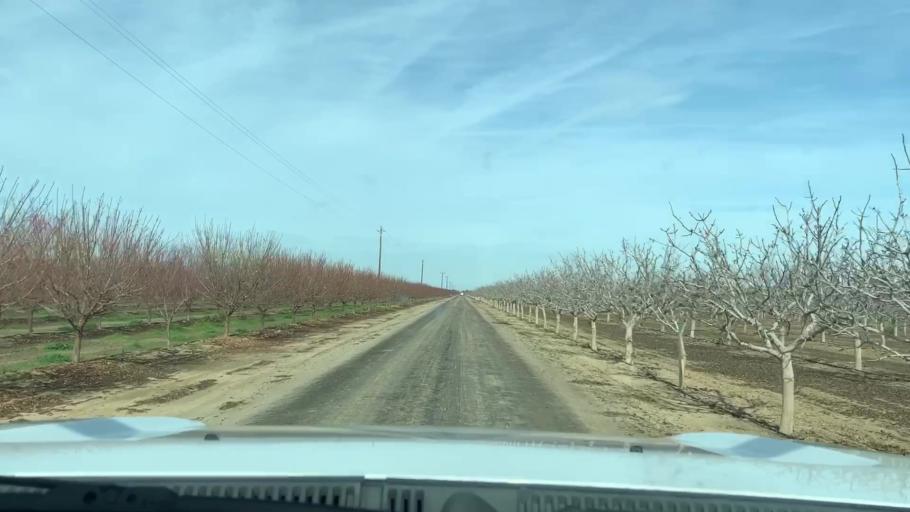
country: US
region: California
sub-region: Kern County
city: Lost Hills
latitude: 35.6031
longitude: -119.5357
